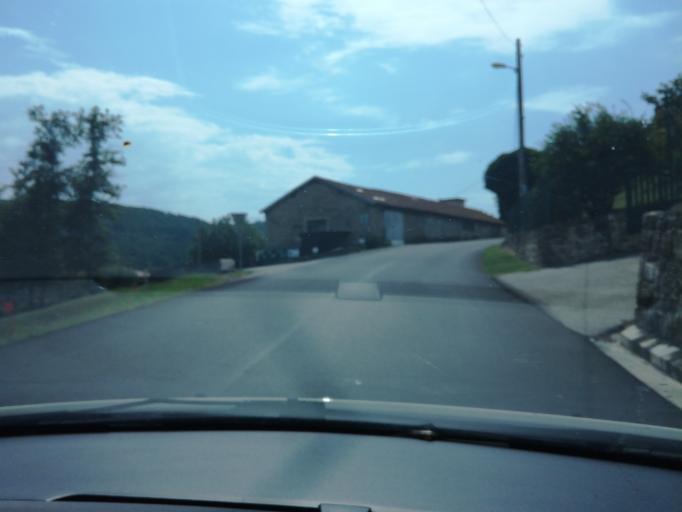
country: FR
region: Rhone-Alpes
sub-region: Departement de l'Ardeche
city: Labegude
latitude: 44.6355
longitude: 4.3639
